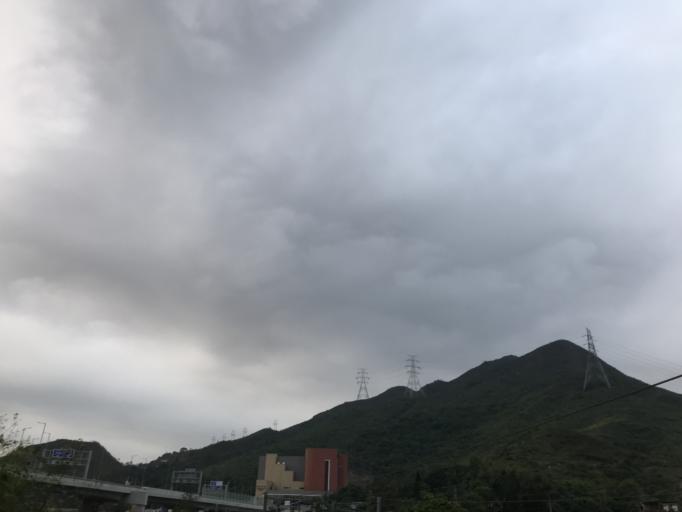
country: HK
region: Tai Po
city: Tai Po
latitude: 22.4807
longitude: 114.1551
